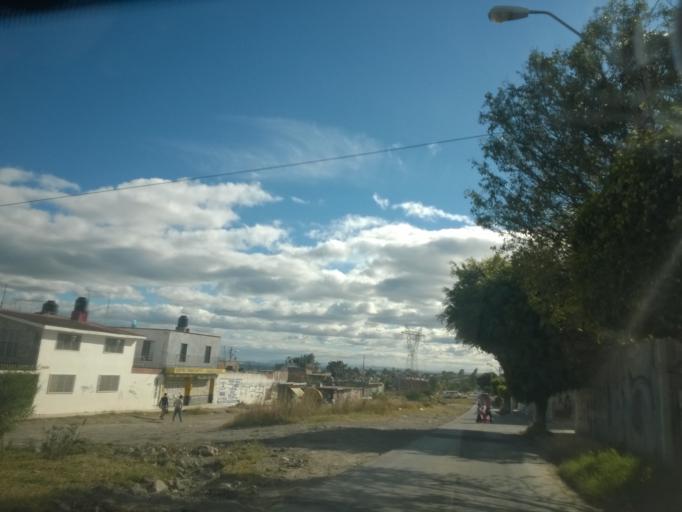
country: MX
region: Guanajuato
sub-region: Leon
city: Ejido la Joya
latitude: 21.1183
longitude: -101.7249
